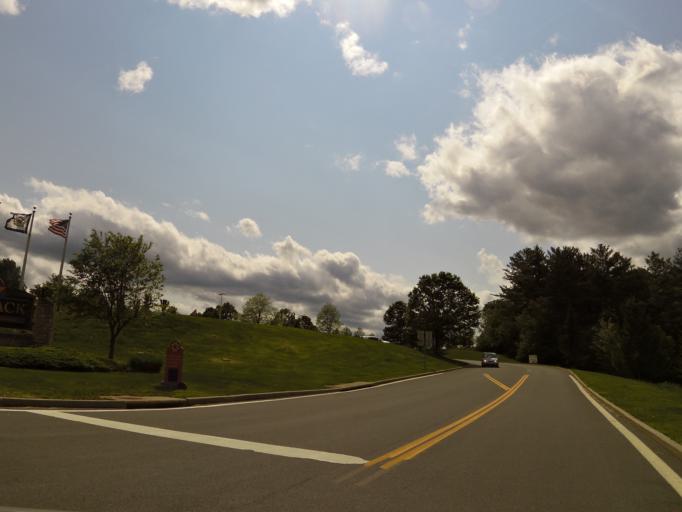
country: US
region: West Virginia
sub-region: Raleigh County
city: Mabscott
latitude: 37.8027
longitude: -81.2156
